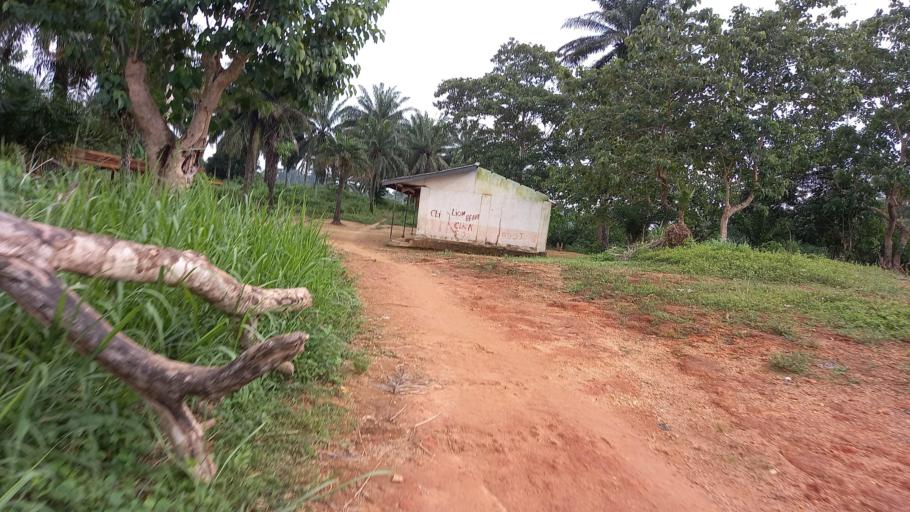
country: SL
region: Eastern Province
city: Kailahun
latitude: 8.2850
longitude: -10.5752
